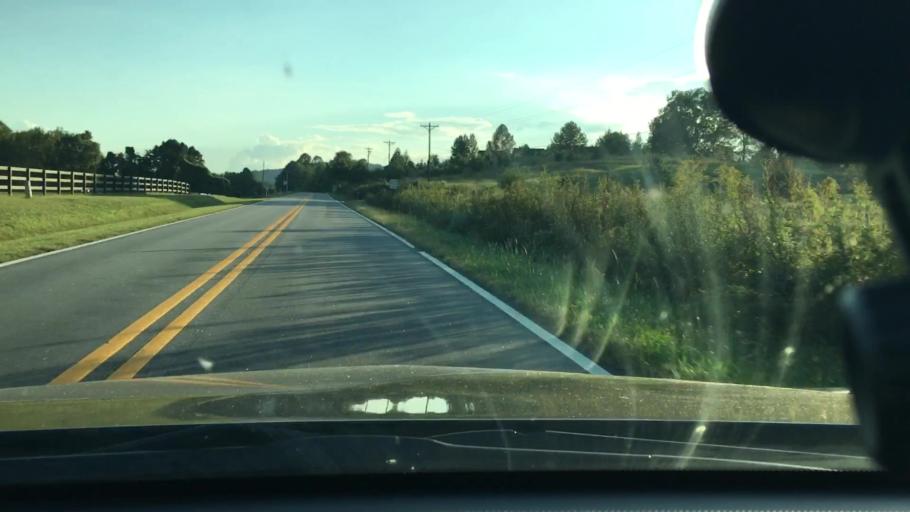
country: US
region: North Carolina
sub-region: Polk County
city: Columbus
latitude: 35.3071
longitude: -82.1516
